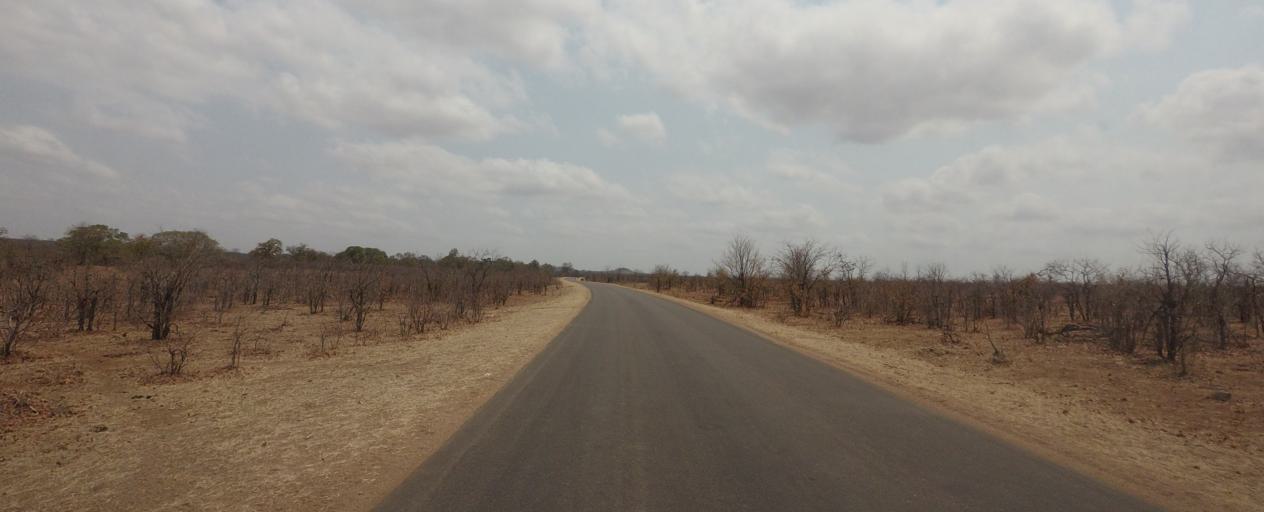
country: ZA
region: Limpopo
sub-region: Mopani District Municipality
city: Phalaborwa
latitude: -23.5416
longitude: 31.4264
